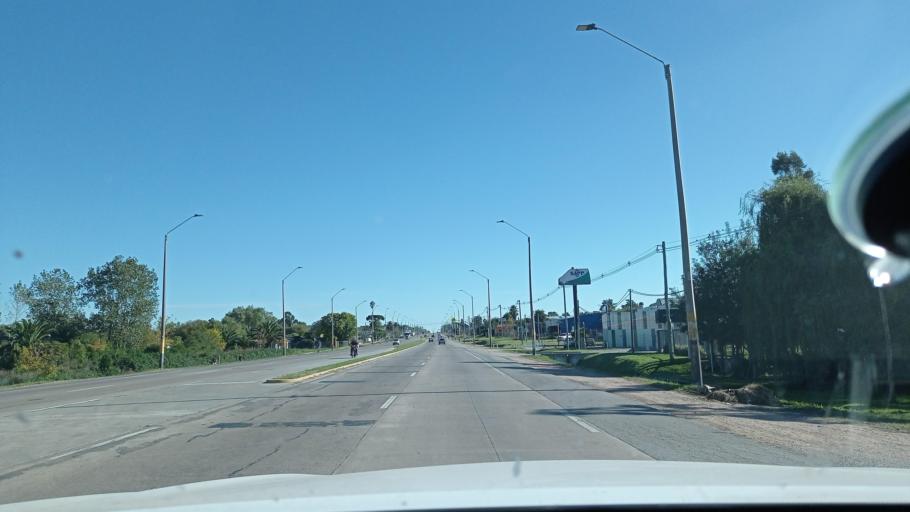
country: UY
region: Canelones
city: Joaquin Suarez
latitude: -34.7563
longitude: -56.0071
